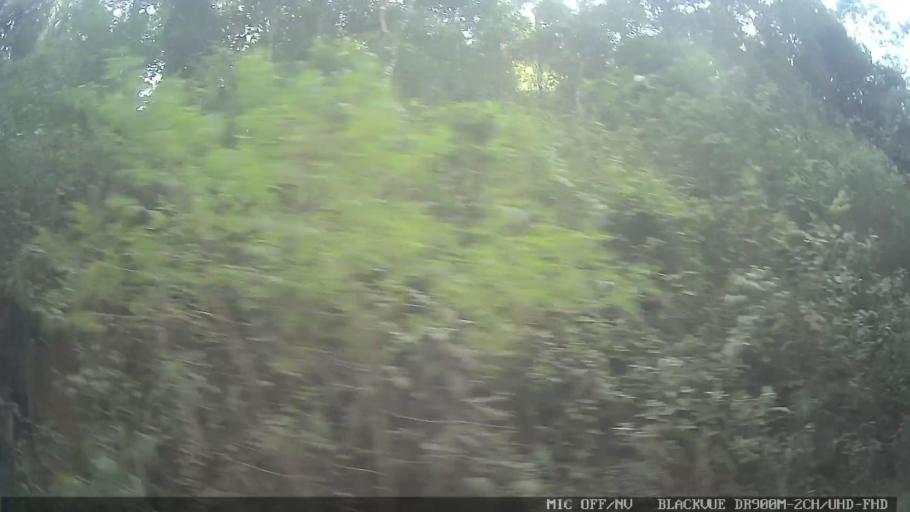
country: BR
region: Sao Paulo
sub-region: Atibaia
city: Atibaia
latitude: -23.1644
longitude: -46.5168
